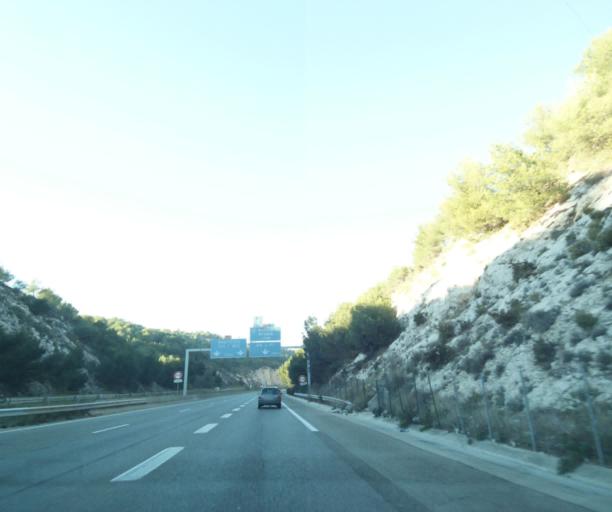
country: FR
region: Provence-Alpes-Cote d'Azur
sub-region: Departement des Bouches-du-Rhone
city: Les Pennes-Mirabeau
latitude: 43.3908
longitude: 5.3022
